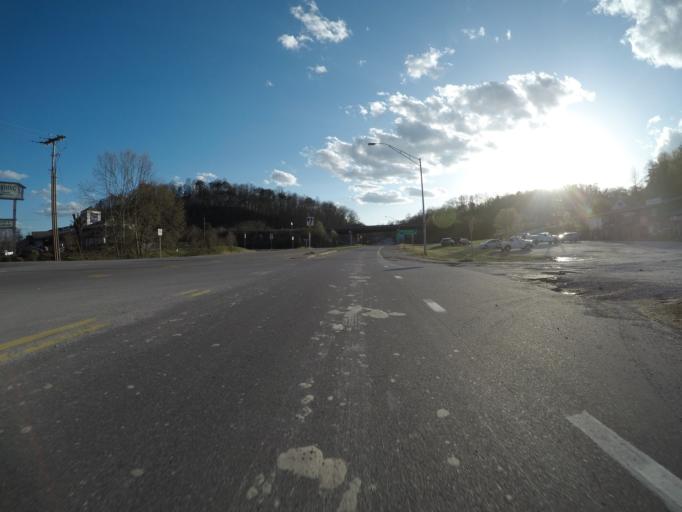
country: US
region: West Virginia
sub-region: Kanawha County
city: Charleston
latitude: 38.3942
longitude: -81.5876
